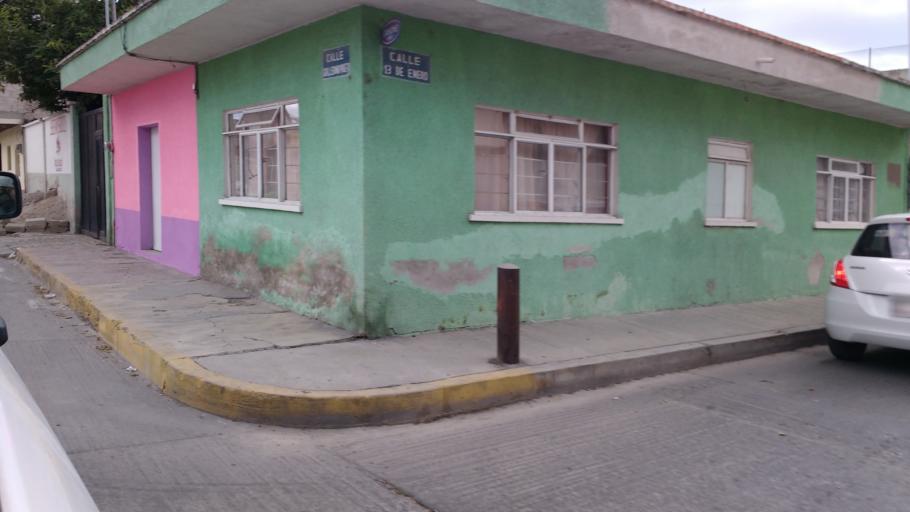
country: MX
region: Hidalgo
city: Mixquiahuala de Juarez
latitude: 20.2270
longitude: -99.2168
